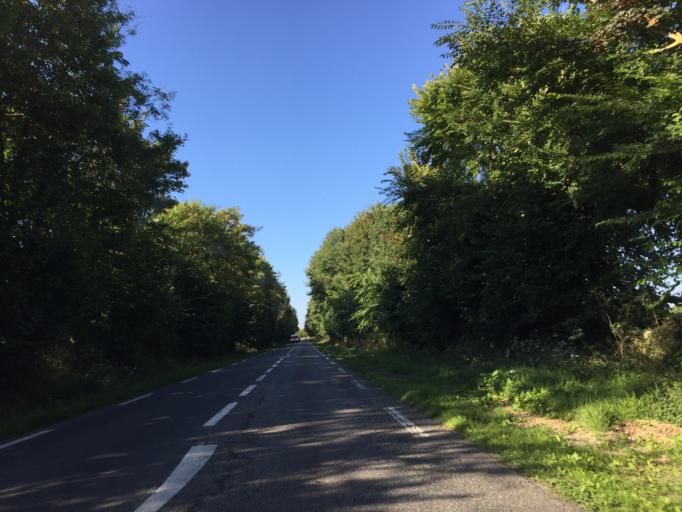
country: FR
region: Lower Normandy
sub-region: Departement du Calvados
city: Equemauville
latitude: 49.3707
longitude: 0.2048
